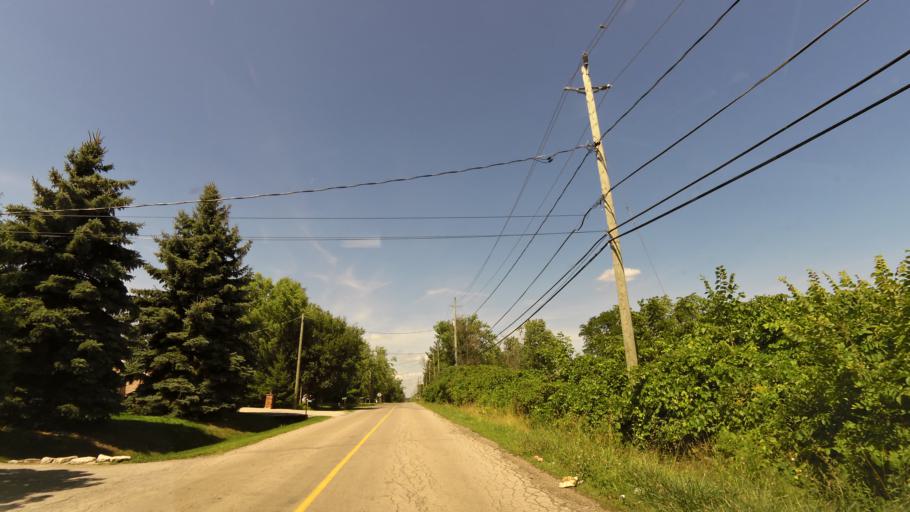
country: CA
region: Ontario
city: Ancaster
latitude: 43.2086
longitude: -79.9453
